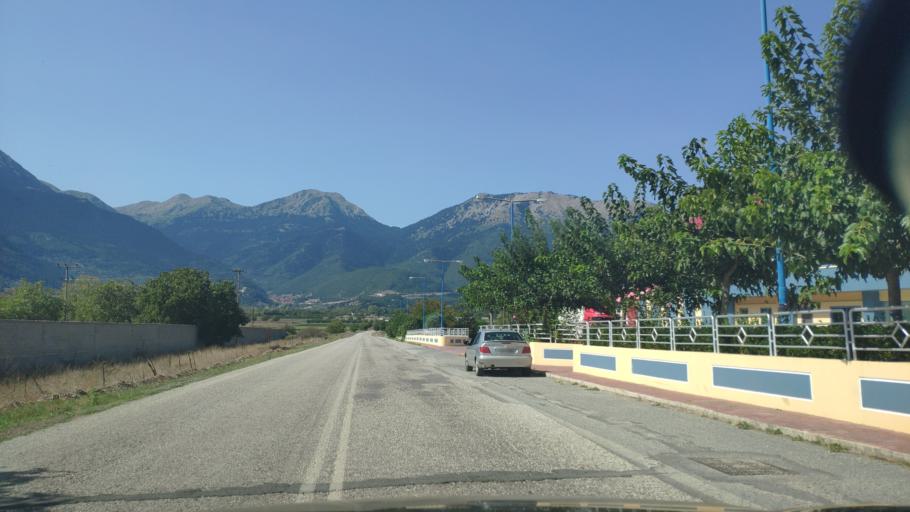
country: GR
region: Peloponnese
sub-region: Nomos Korinthias
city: Nemea
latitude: 37.8493
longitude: 22.4296
